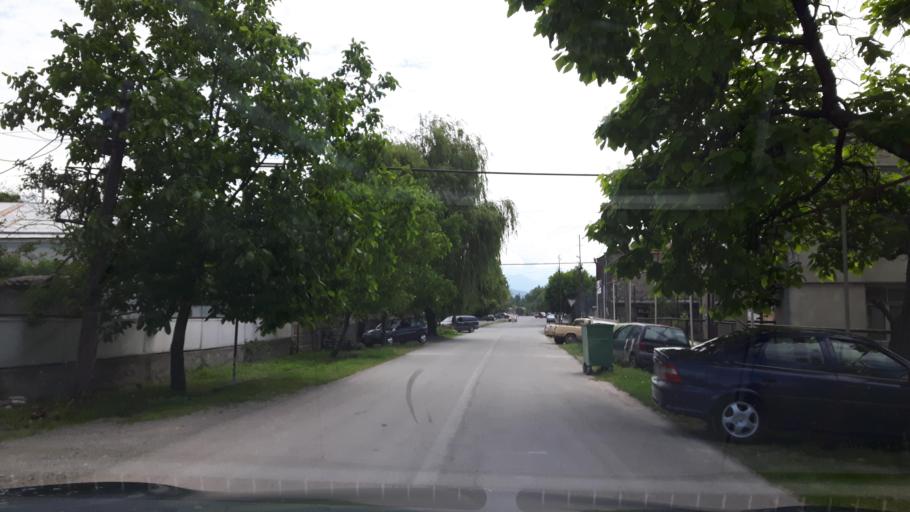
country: GE
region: Kakheti
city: Akhmet'a
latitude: 42.0337
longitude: 45.2077
